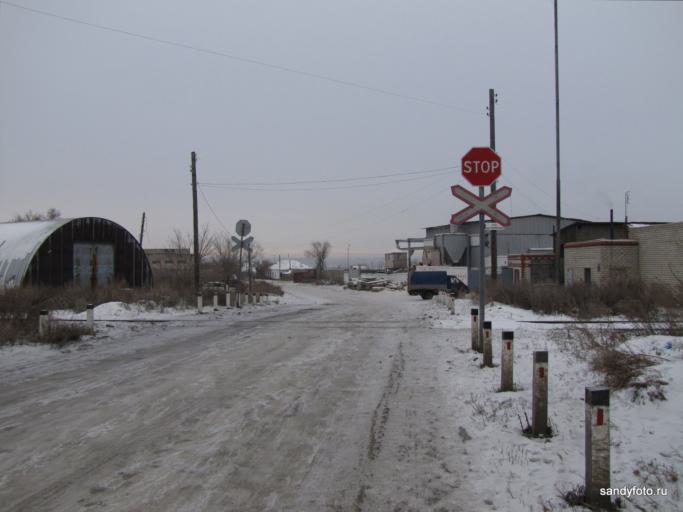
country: RU
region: Chelyabinsk
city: Troitsk
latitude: 54.1025
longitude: 61.5744
